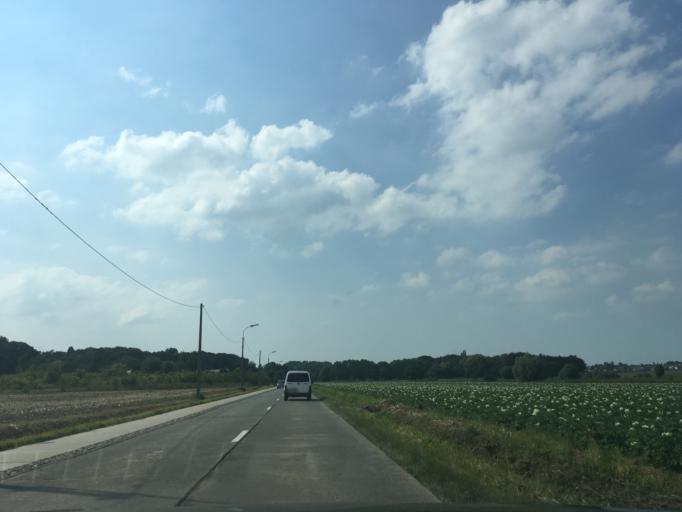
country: BE
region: Flanders
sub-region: Provincie West-Vlaanderen
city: Houthulst
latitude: 50.9731
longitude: 2.9670
